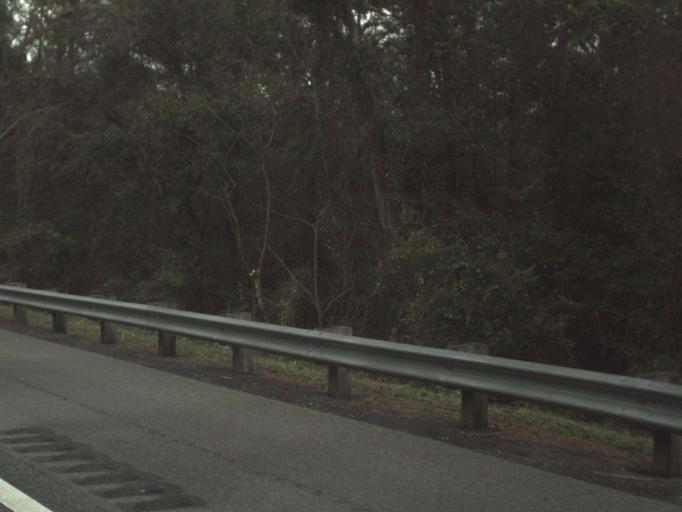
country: US
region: Florida
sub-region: Gadsden County
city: Midway
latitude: 30.5281
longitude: -84.5021
